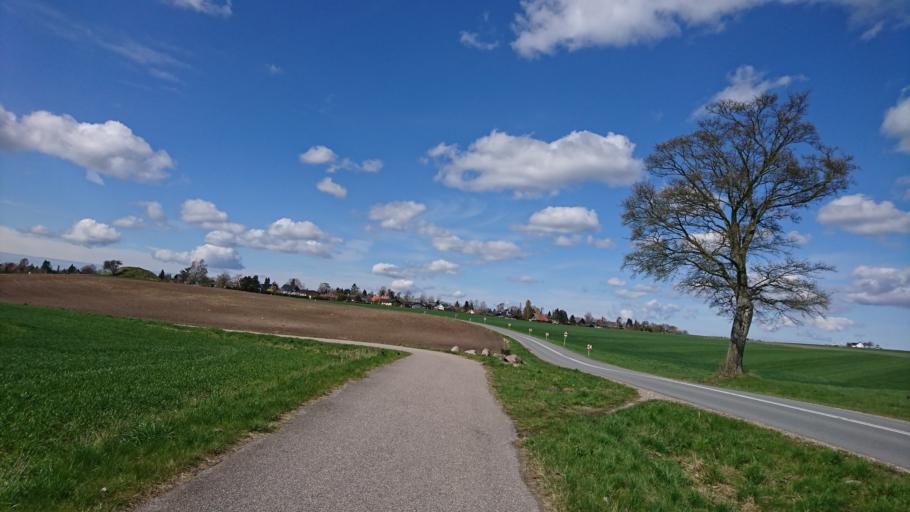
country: DK
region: Capital Region
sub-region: Egedal Kommune
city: Ganlose
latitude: 55.7847
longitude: 12.2773
